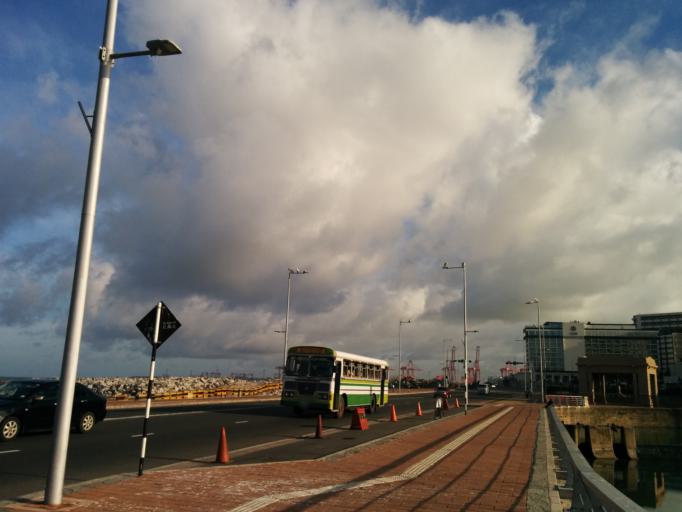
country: LK
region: Western
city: Colombo
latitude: 6.9297
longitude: 79.8428
